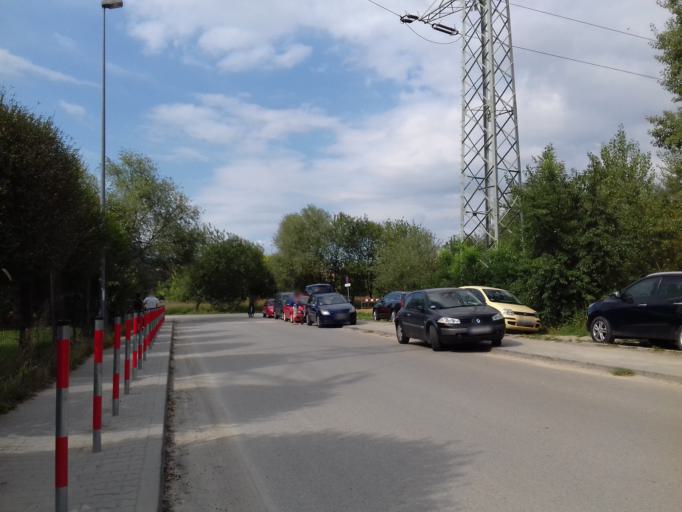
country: PL
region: Lesser Poland Voivodeship
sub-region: Krakow
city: Krakow
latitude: 50.0815
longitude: 19.9940
